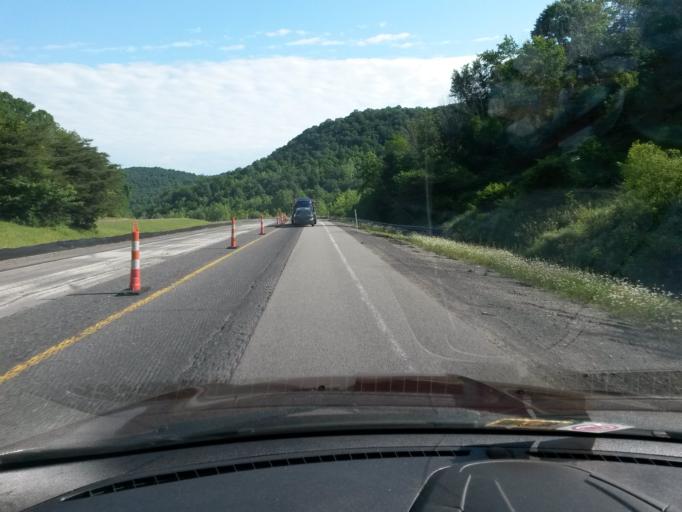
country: US
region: West Virginia
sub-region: Braxton County
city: Sutton
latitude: 38.7513
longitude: -80.6768
